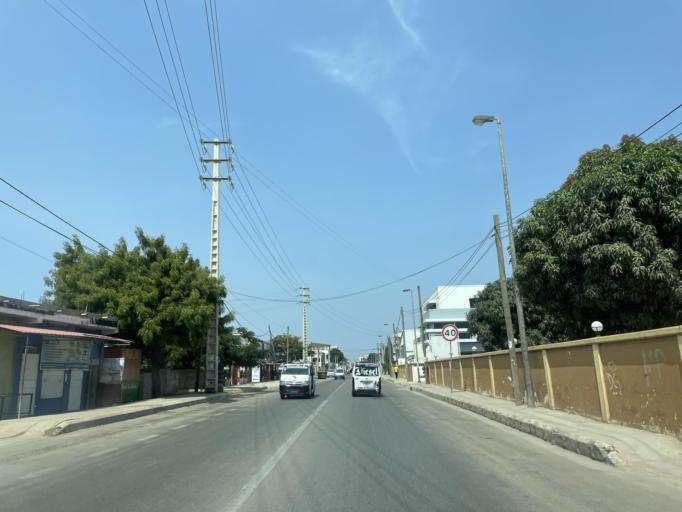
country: AO
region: Luanda
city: Luanda
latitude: -8.8964
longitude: 13.1907
